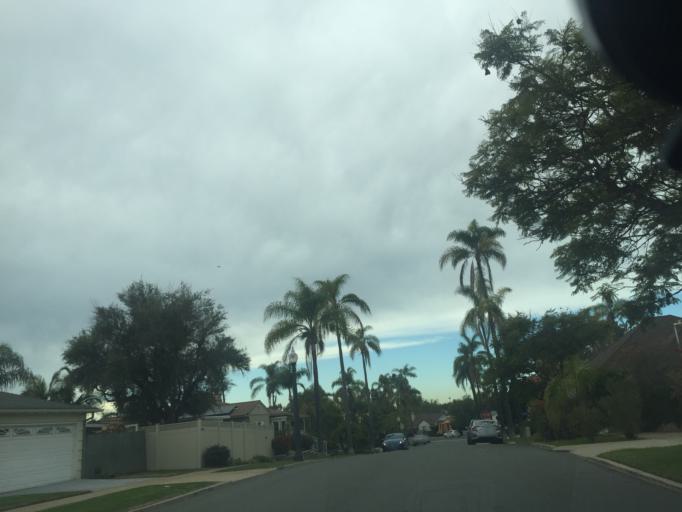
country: US
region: California
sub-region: San Diego County
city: Lemon Grove
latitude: 32.7610
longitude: -117.0928
